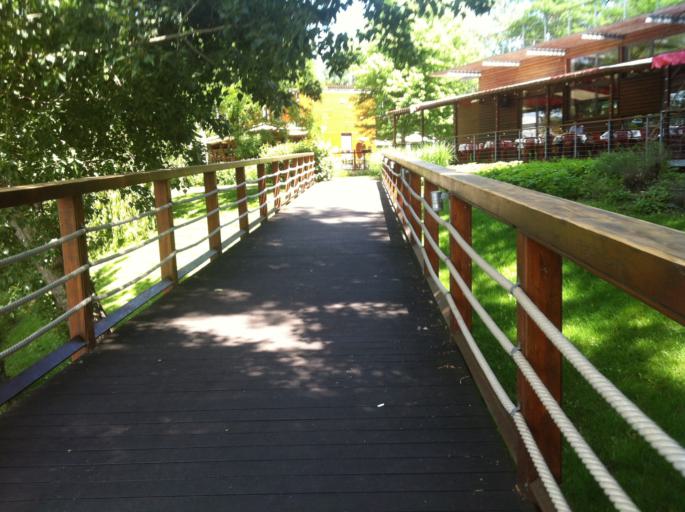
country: HU
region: Budapest
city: Budapest IX. keruelet
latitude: 47.4612
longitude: 19.0597
